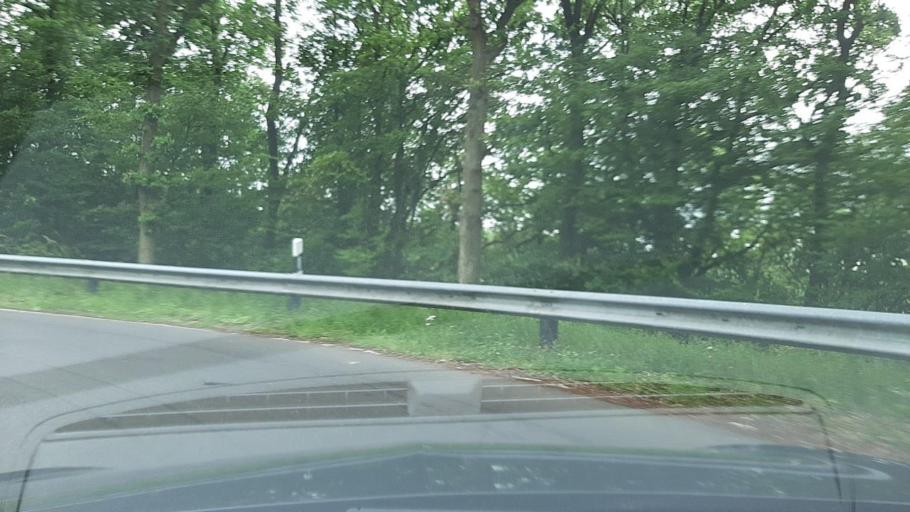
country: DE
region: Rheinland-Pfalz
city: Beltheim
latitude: 50.0961
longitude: 7.4549
